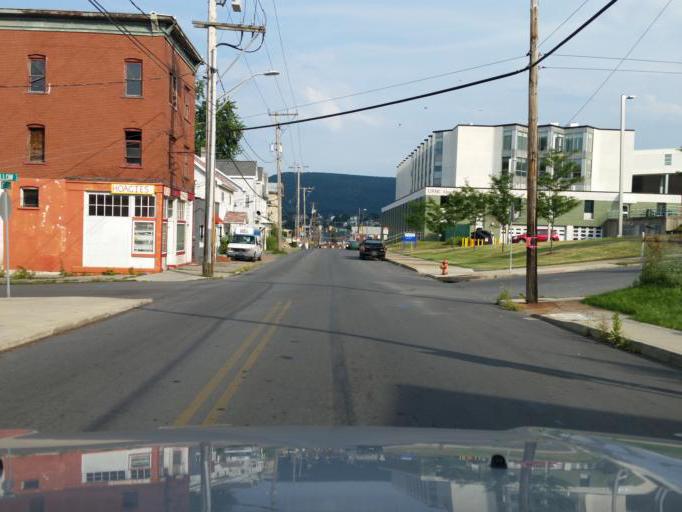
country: US
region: Pennsylvania
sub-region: Blair County
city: Altoona
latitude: 40.5242
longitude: -78.3984
